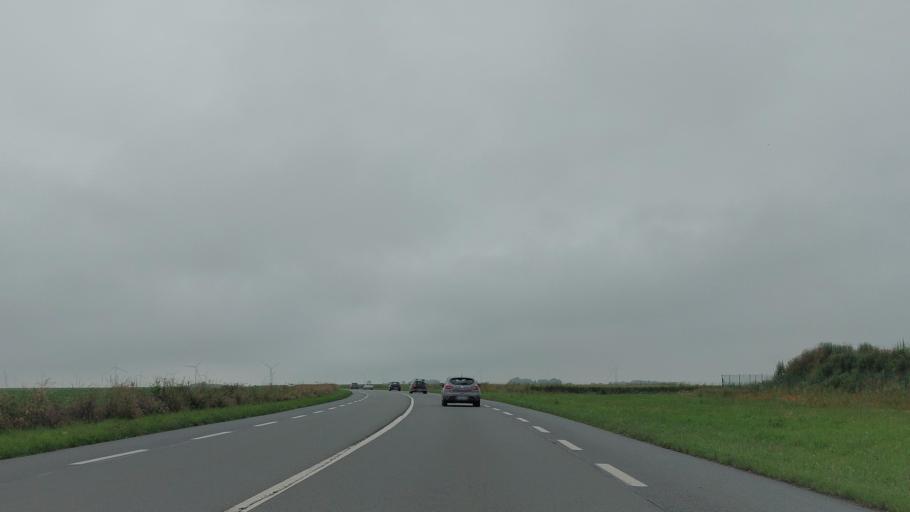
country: FR
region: Picardie
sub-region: Departement de la Somme
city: Woincourt
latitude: 50.0737
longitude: 1.5336
